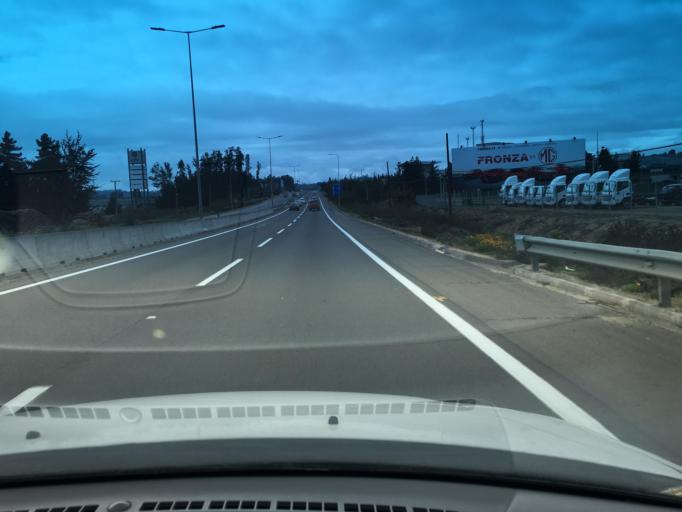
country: CL
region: Valparaiso
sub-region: Provincia de Valparaiso
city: Vina del Mar
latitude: -33.1359
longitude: -71.5625
